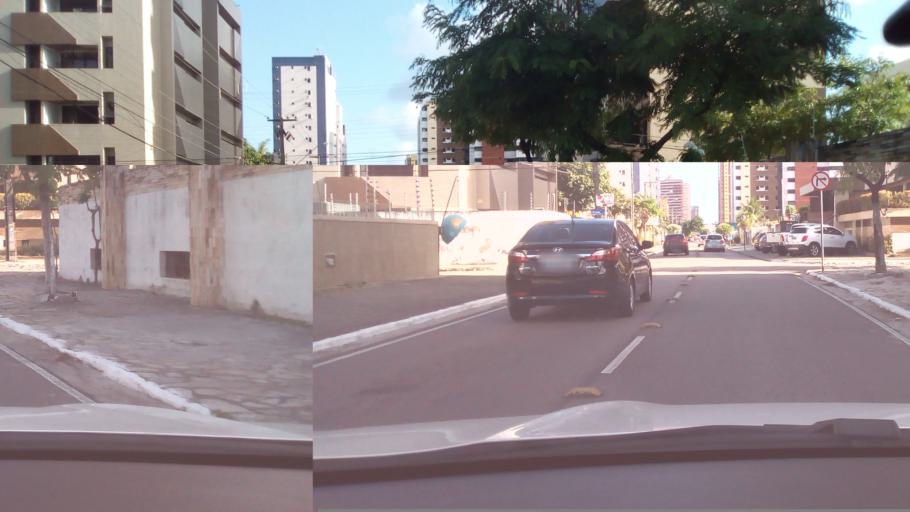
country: BR
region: Paraiba
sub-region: Joao Pessoa
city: Joao Pessoa
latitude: -7.1046
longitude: -34.8386
